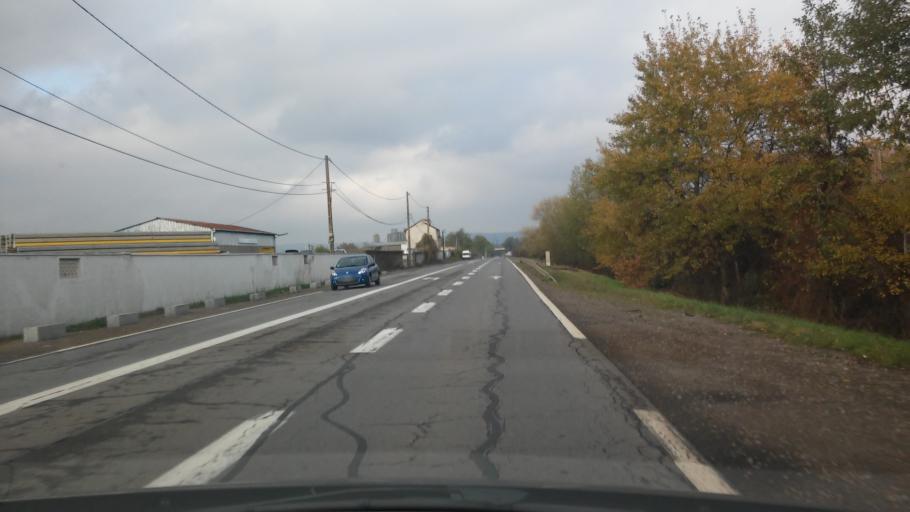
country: FR
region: Lorraine
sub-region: Departement de la Moselle
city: Uckange
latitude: 49.3193
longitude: 6.1556
